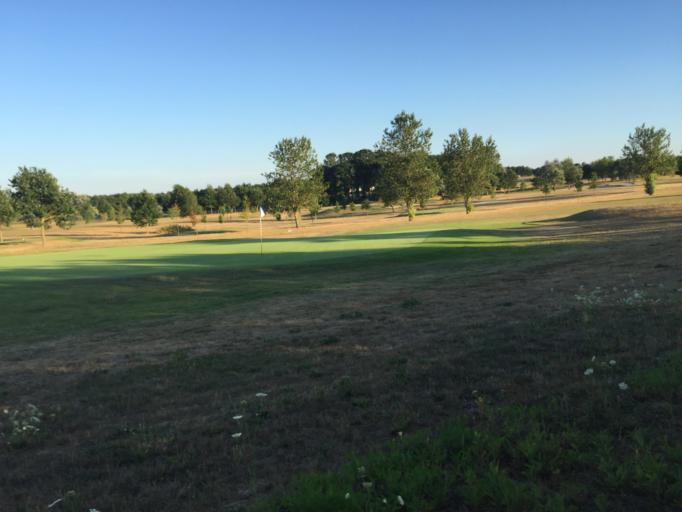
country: DK
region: South Denmark
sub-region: Odense Kommune
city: Bellinge
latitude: 55.3800
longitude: 10.3260
